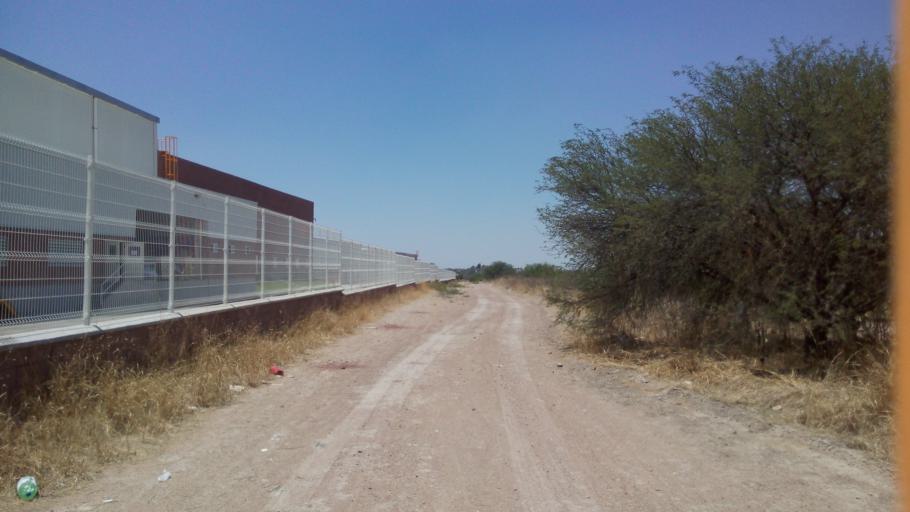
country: MX
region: Aguascalientes
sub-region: Aguascalientes
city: San Sebastian [Fraccionamiento]
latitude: 21.7986
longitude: -102.2979
